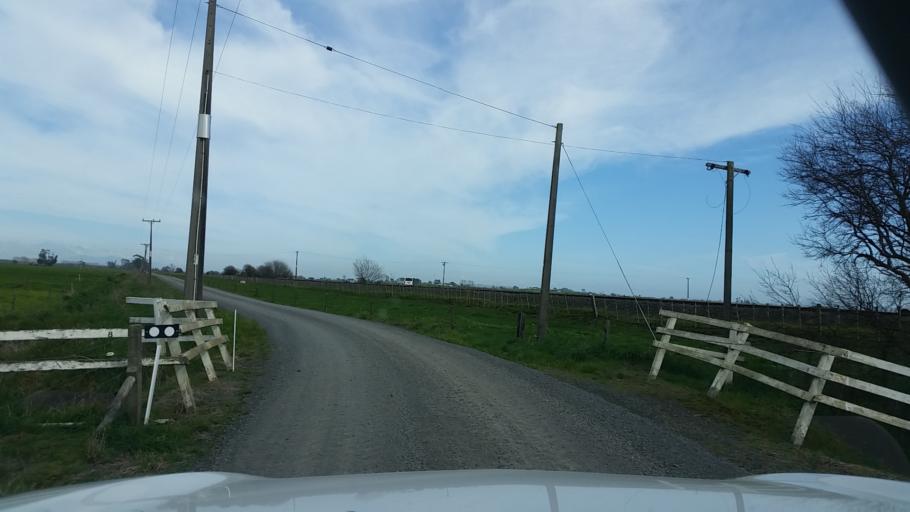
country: NZ
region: Waikato
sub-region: Waipa District
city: Cambridge
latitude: -37.6772
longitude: 175.4619
